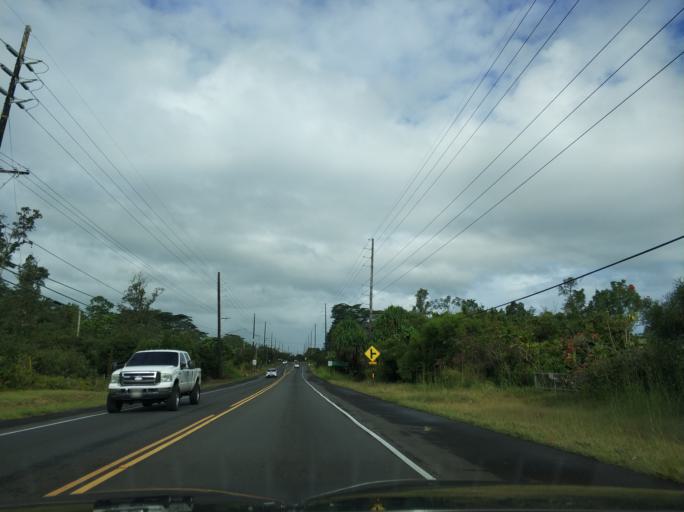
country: US
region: Hawaii
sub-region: Hawaii County
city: Orchidlands Estates
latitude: 19.5679
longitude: -154.9979
